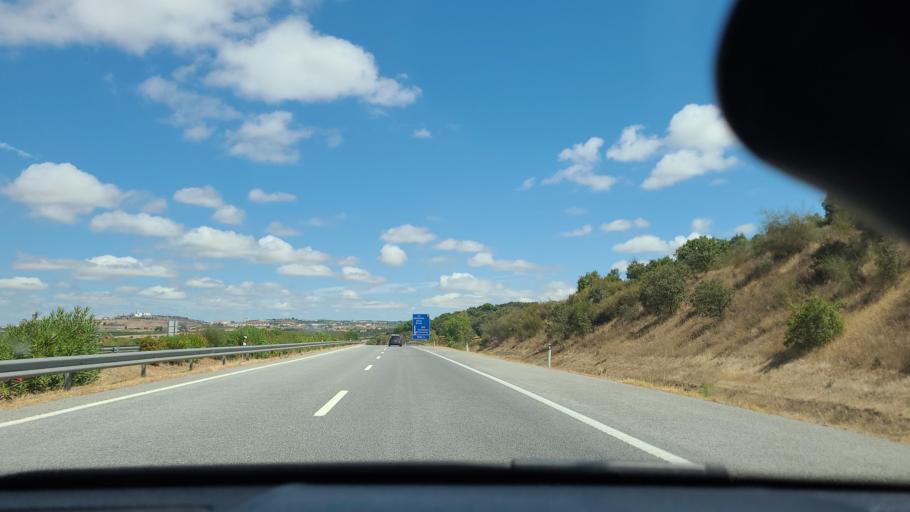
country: PT
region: Evora
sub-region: Estremoz
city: Estremoz
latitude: 38.8112
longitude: -7.6205
